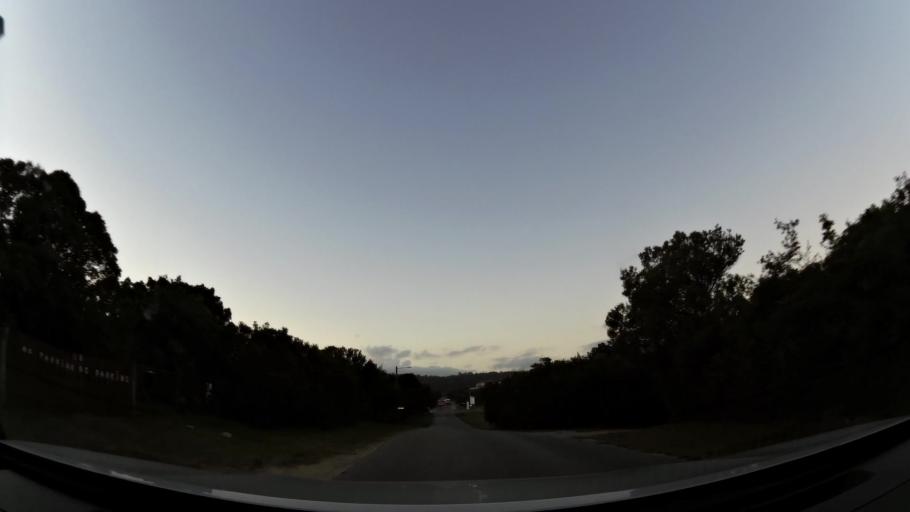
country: ZA
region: Western Cape
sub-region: Eden District Municipality
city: Knysna
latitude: -34.0275
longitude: 22.8067
